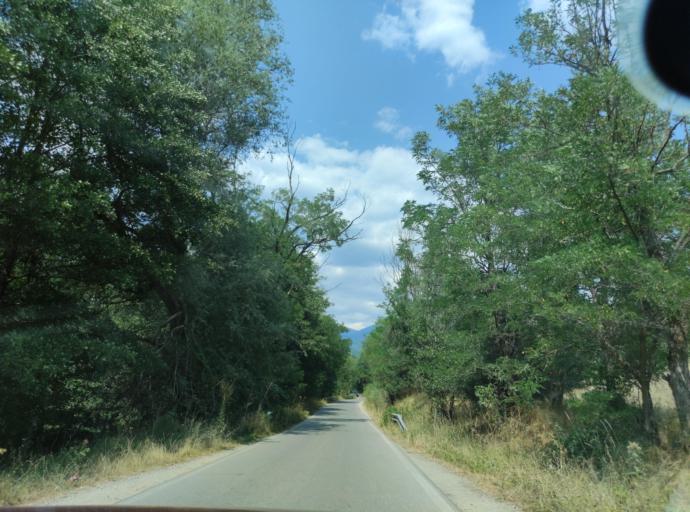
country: BG
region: Blagoevgrad
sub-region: Obshtina Belitsa
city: Belitsa
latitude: 41.9772
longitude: 23.5536
